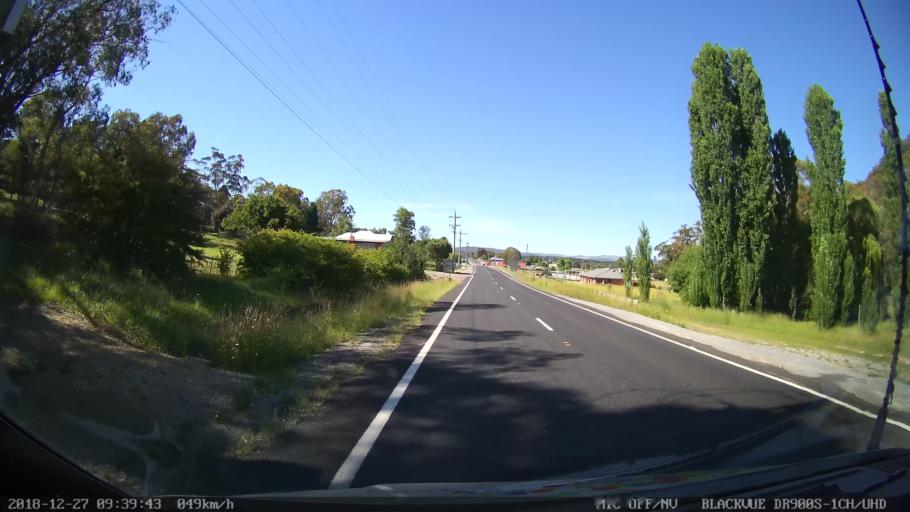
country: AU
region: New South Wales
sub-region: Lithgow
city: Portland
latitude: -33.2954
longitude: 150.0343
